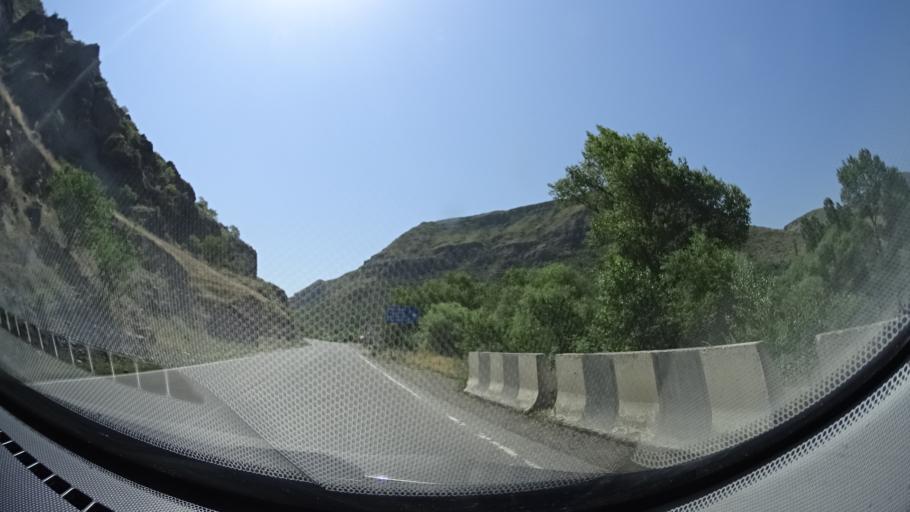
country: GE
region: Samtskhe-Javakheti
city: Aspindza
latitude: 41.4855
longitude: 43.2683
